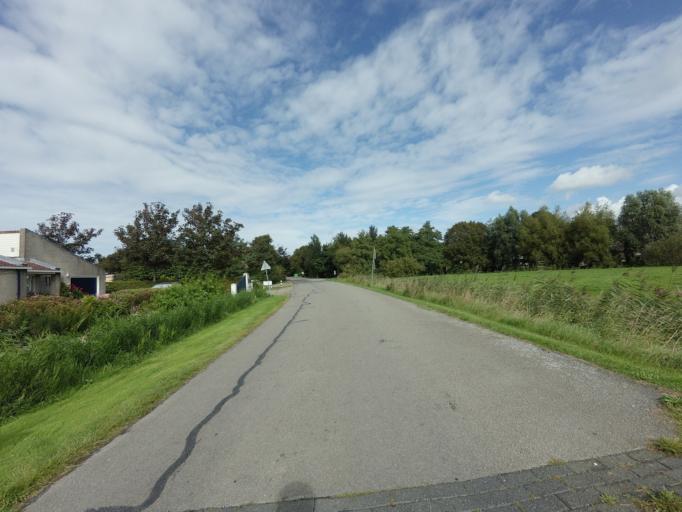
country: NL
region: Friesland
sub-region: Sudwest Fryslan
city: Makkum
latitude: 53.0821
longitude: 5.4260
